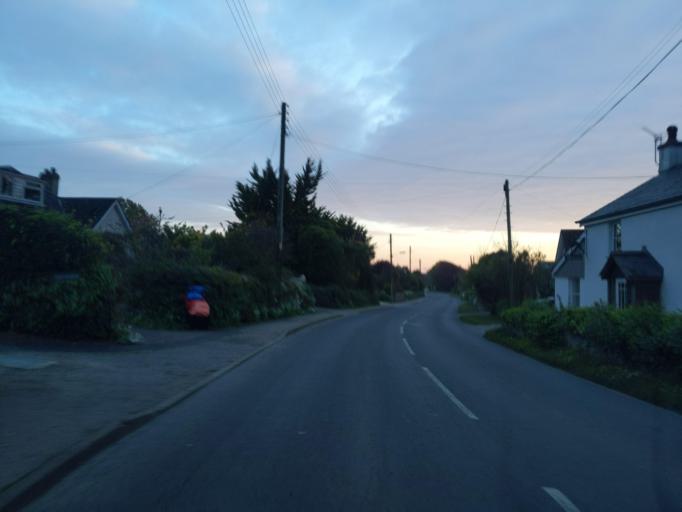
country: GB
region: England
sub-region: Cornwall
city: Polzeath
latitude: 50.5522
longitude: -4.8980
